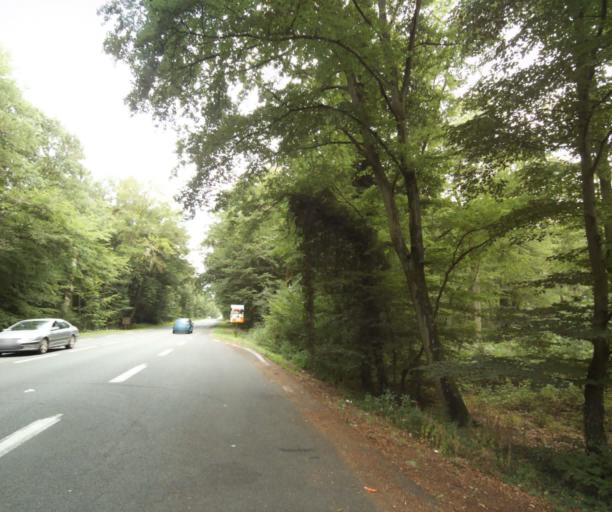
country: FR
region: Ile-de-France
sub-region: Departement de Seine-et-Marne
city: Bois-le-Roi
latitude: 48.4730
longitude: 2.6791
